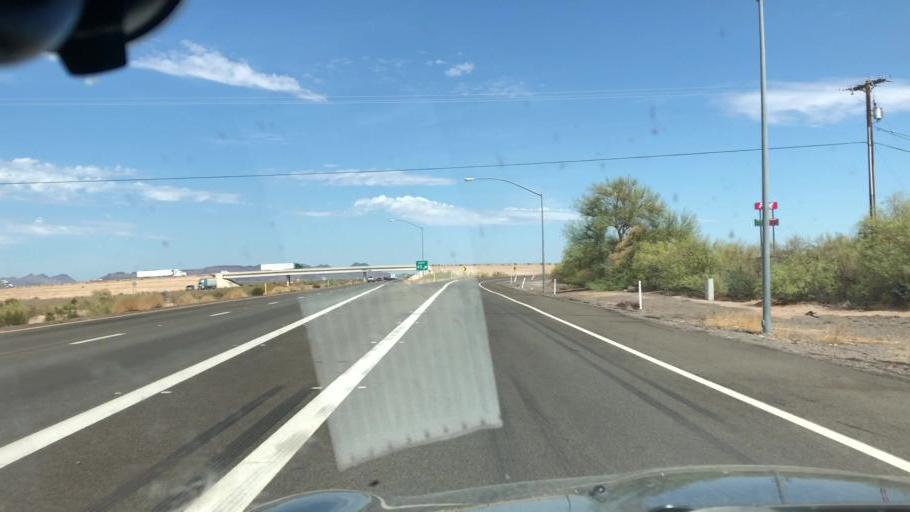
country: US
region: Arizona
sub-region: La Paz County
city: Salome
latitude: 33.6311
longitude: -113.7721
